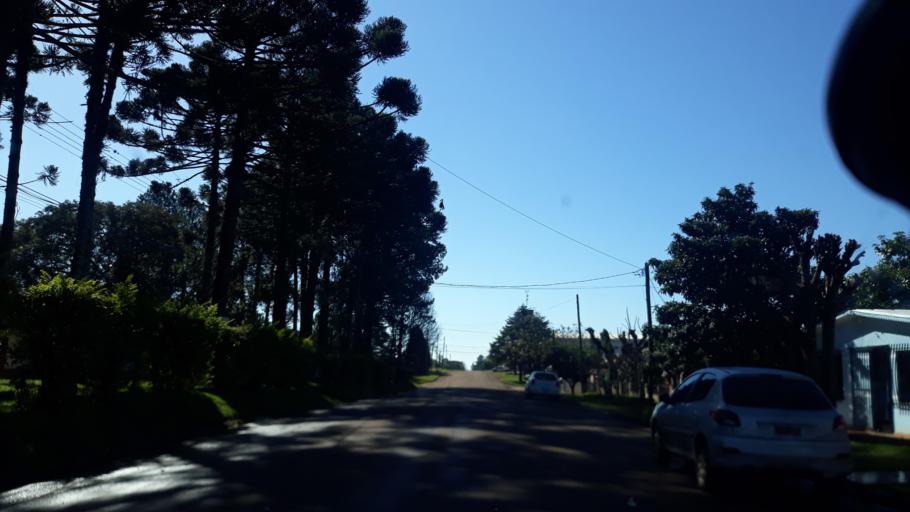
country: AR
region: Misiones
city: Bernardo de Irigoyen
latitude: -26.2640
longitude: -53.6515
